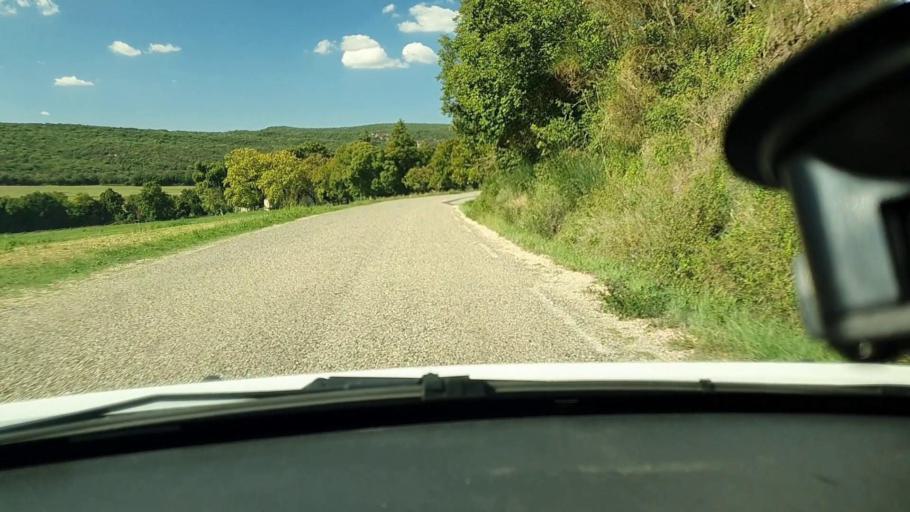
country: FR
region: Languedoc-Roussillon
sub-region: Departement du Gard
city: Goudargues
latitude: 44.1408
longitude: 4.4518
